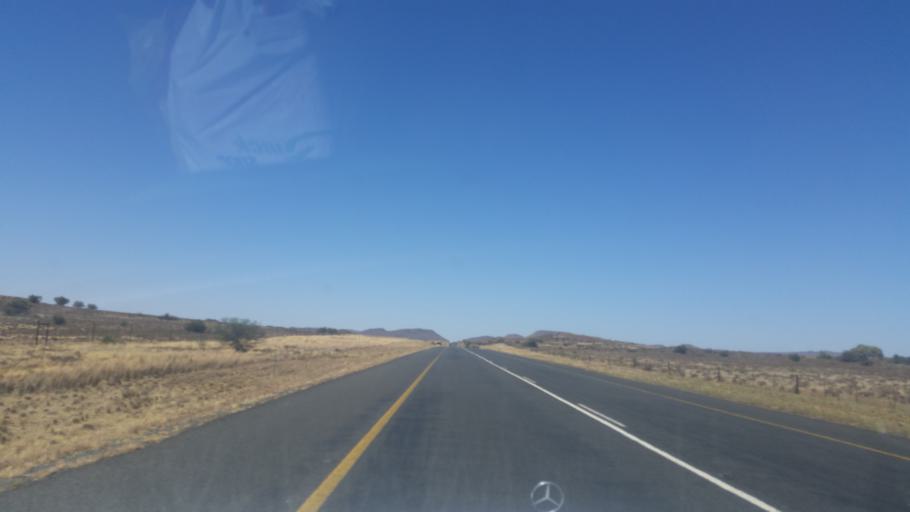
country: ZA
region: Northern Cape
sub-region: Pixley ka Seme District Municipality
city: Colesberg
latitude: -30.6178
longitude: 25.3118
